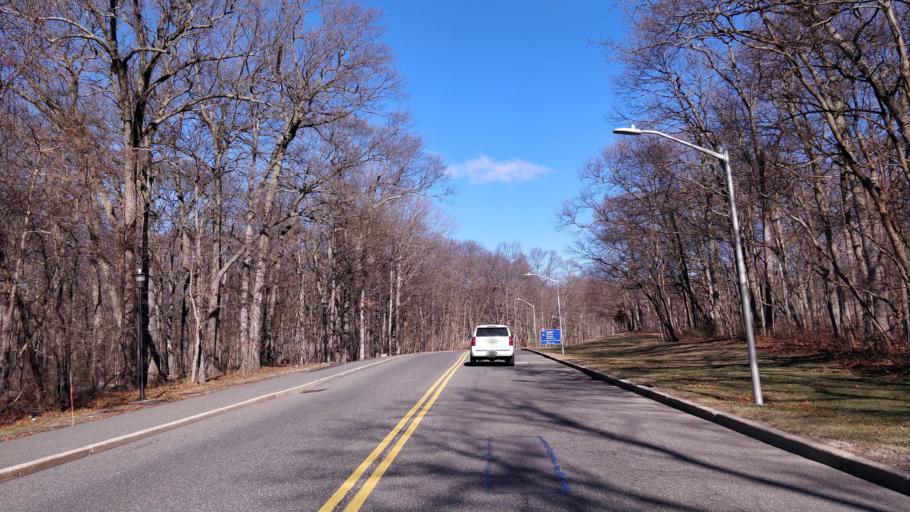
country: US
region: New York
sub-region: Suffolk County
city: Stony Brook
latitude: 40.9000
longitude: -73.1237
